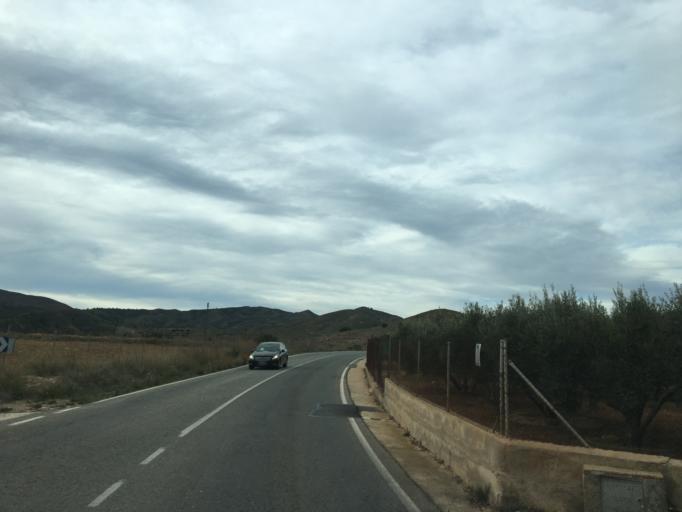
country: ES
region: Murcia
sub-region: Murcia
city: Fuente-Alamo de Murcia
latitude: 37.6135
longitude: -1.0980
